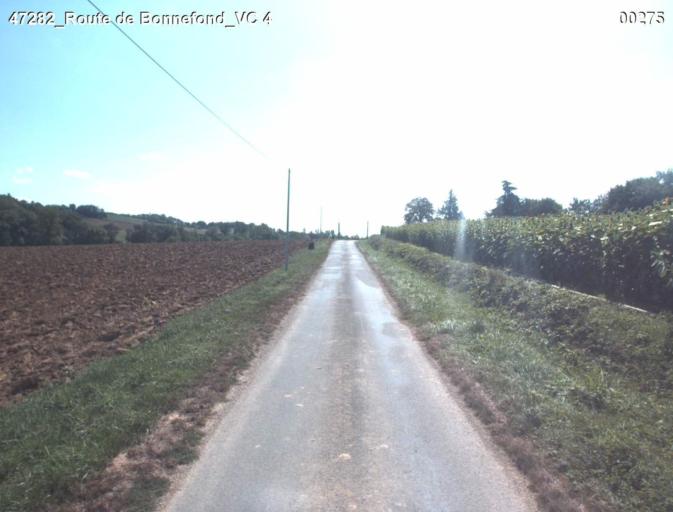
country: FR
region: Aquitaine
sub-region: Departement du Lot-et-Garonne
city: Laplume
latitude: 44.1071
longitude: 0.4755
